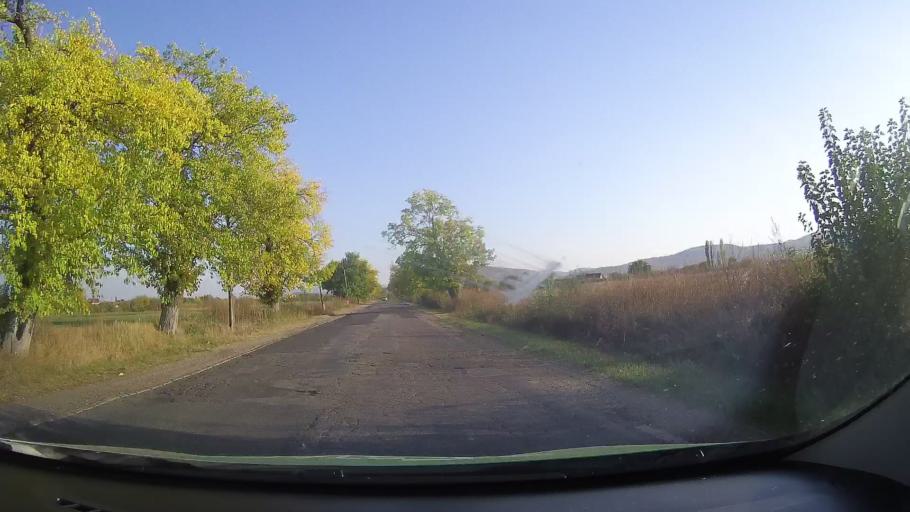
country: RO
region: Arad
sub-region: Comuna Pancota
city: Maderat
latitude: 46.3074
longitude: 21.7071
